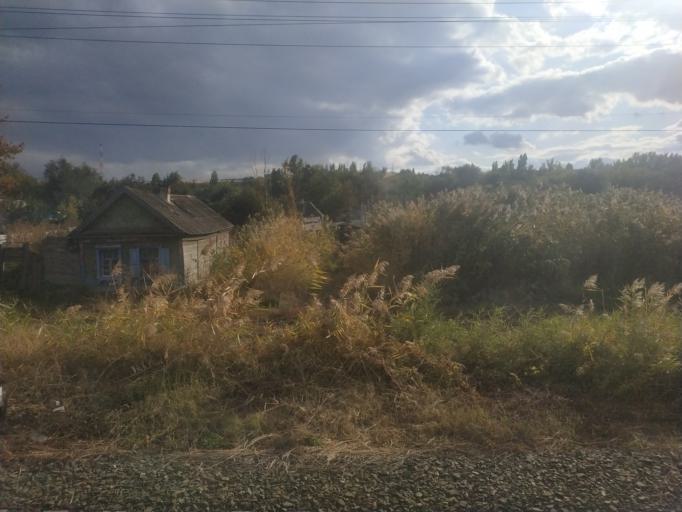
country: RU
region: Volgograd
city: Krasnoslobodsk
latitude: 48.5096
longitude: 44.5327
